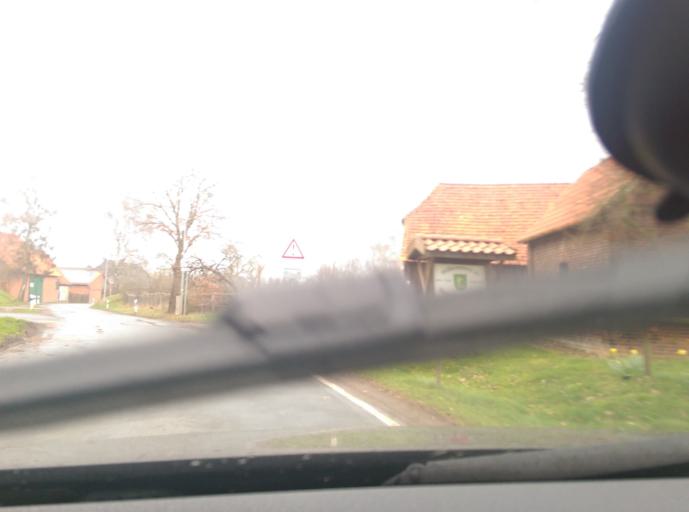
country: DE
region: Lower Saxony
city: Schwarmstedt
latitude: 52.6222
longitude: 9.6016
